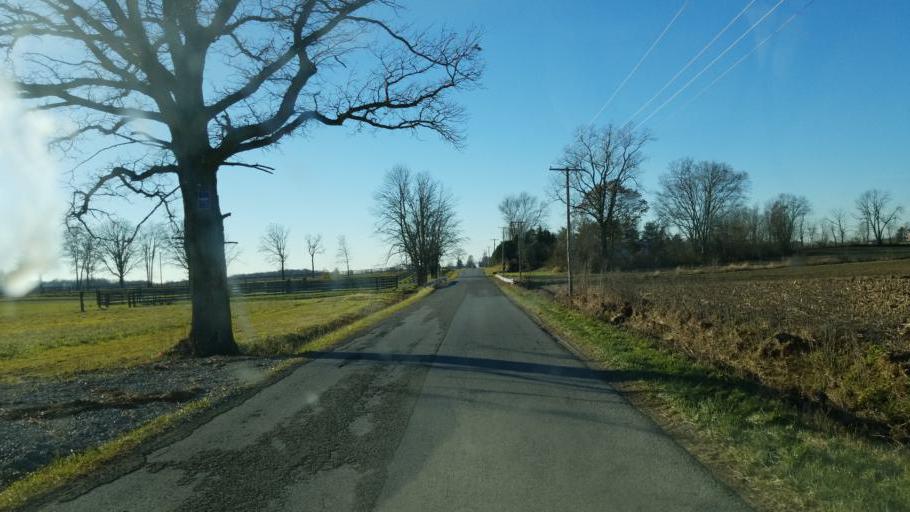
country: US
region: Ohio
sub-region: Morrow County
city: Cardington
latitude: 40.4672
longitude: -82.8976
